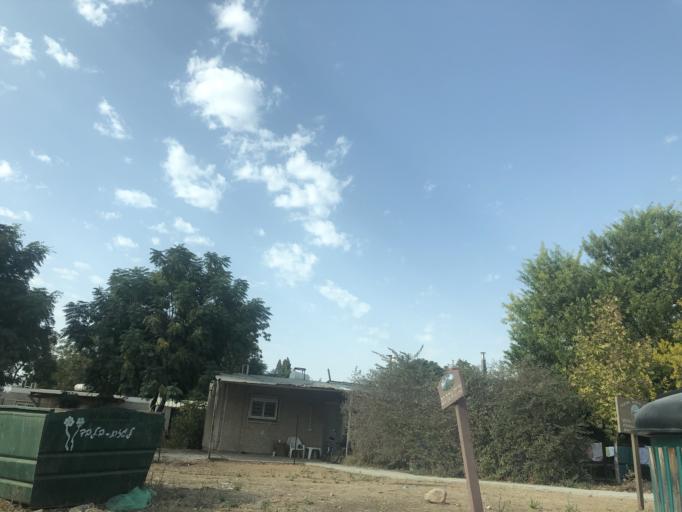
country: IL
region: Central District
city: Rosh Ha'Ayin
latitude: 32.0803
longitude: 34.9375
